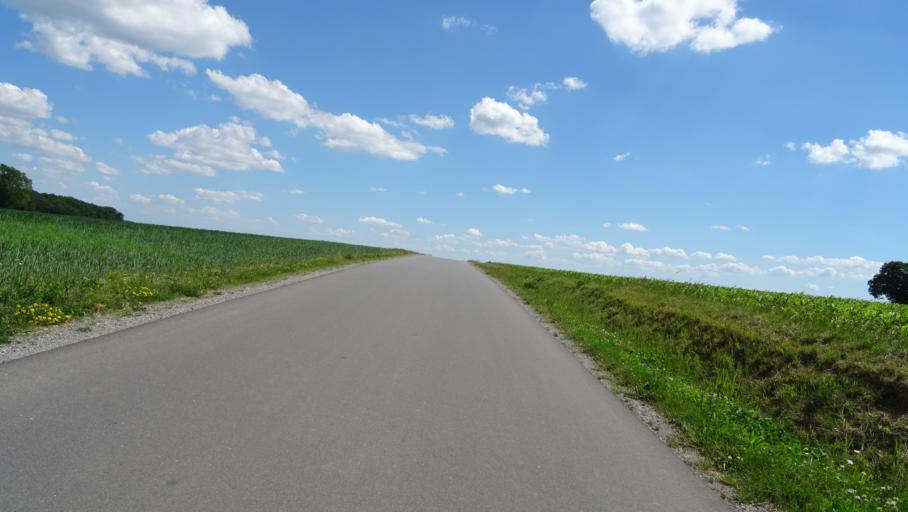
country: DE
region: Baden-Wuerttemberg
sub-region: Karlsruhe Region
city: Adelsheim
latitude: 49.3992
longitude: 9.3674
